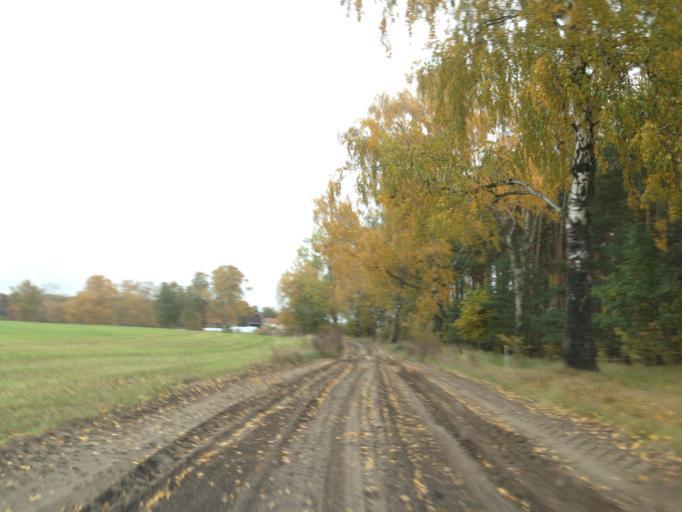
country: PL
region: Pomeranian Voivodeship
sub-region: Powiat kwidzynski
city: Prabuty
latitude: 53.7286
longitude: 19.2091
